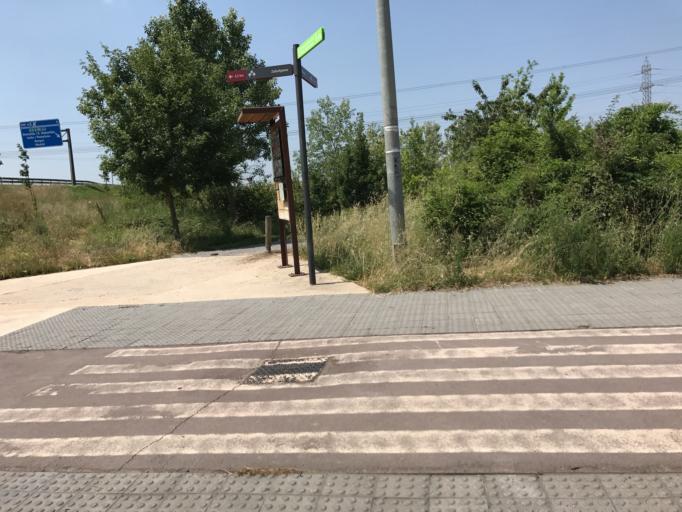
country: ES
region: Basque Country
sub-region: Provincia de Alava
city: Gasteiz / Vitoria
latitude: 42.8733
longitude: -2.6904
